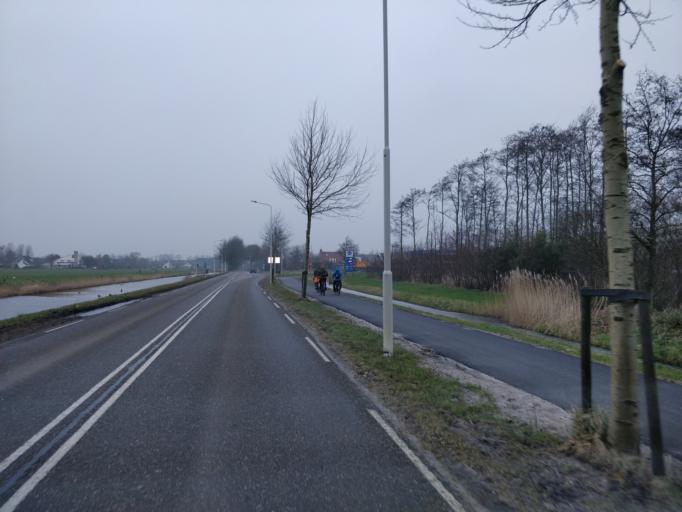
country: NL
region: Friesland
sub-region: Gemeente Het Bildt
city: Sint Annaparochie
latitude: 53.2674
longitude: 5.6591
